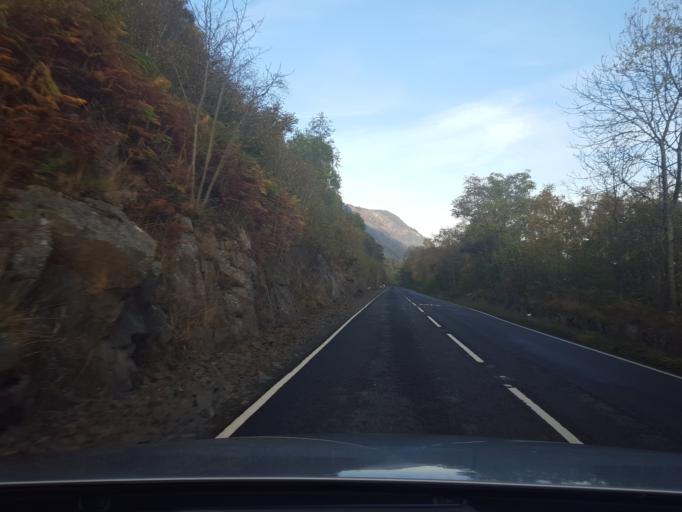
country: GB
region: Scotland
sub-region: Highland
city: Beauly
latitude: 57.3711
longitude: -4.3863
